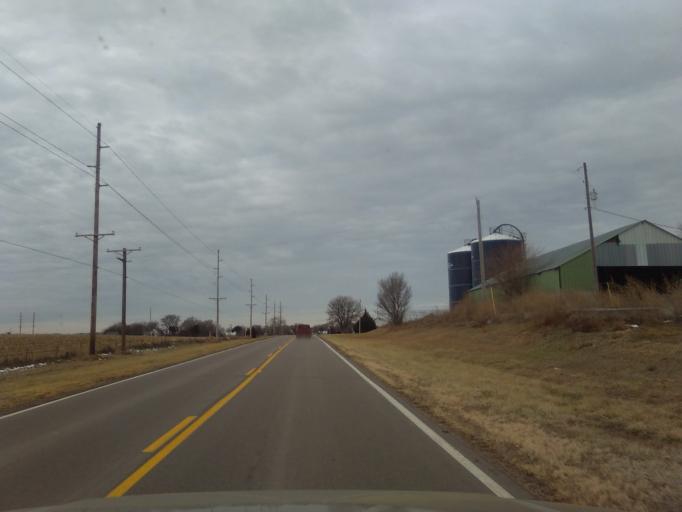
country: US
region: Nebraska
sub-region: Hall County
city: Grand Island
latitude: 40.7710
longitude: -98.3543
